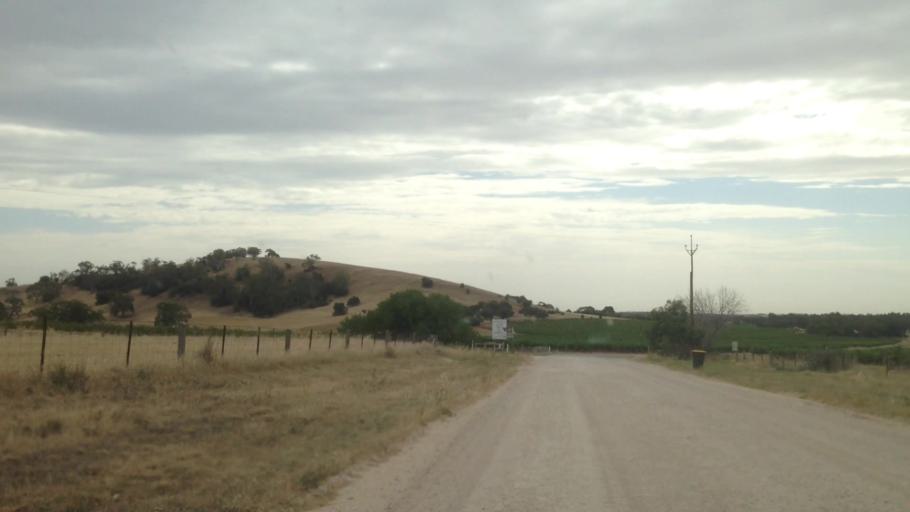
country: AU
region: South Australia
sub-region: Barossa
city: Lyndoch
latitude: -34.5990
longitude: 138.9289
